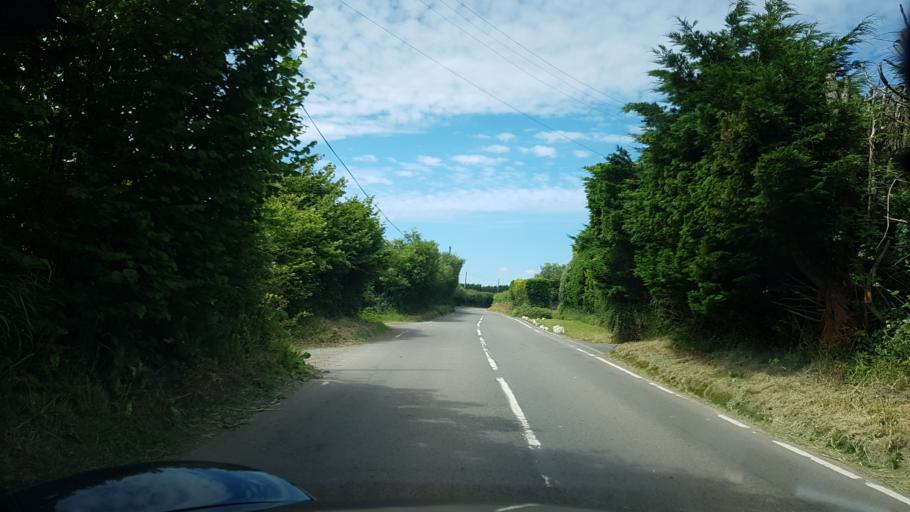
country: GB
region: Wales
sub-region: Carmarthenshire
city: Whitland
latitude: 51.7730
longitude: -4.5995
